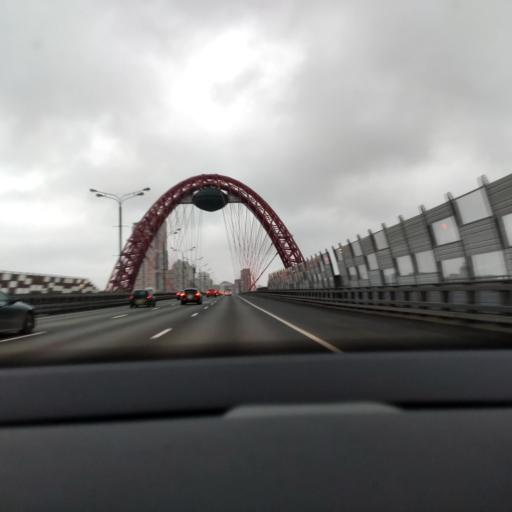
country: RU
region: Moscow
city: Shchukino
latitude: 55.7739
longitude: 37.4397
